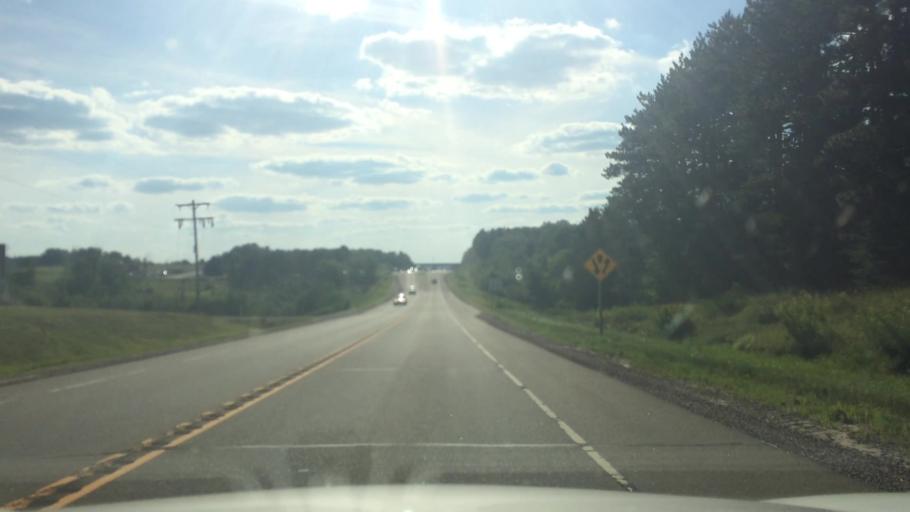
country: US
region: Wisconsin
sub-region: Lincoln County
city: Merrill
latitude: 45.1779
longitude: -89.6360
